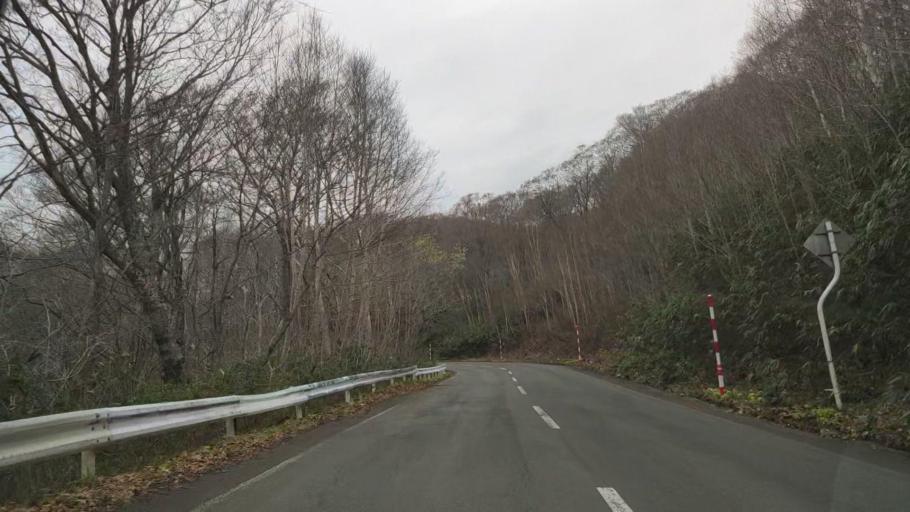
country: JP
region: Akita
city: Hanawa
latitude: 40.4184
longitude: 140.8378
